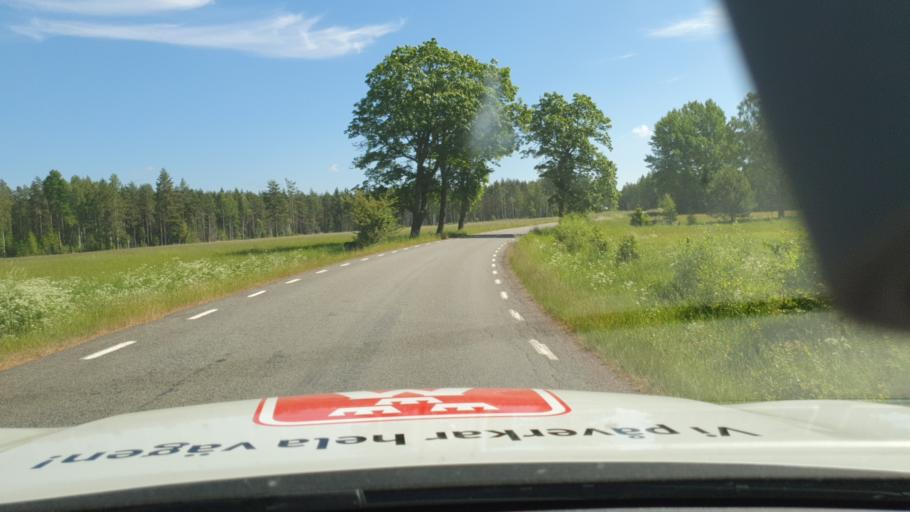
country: SE
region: Vaestra Goetaland
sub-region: Tidaholms Kommun
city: Olofstorp
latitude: 58.2750
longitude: 13.9591
